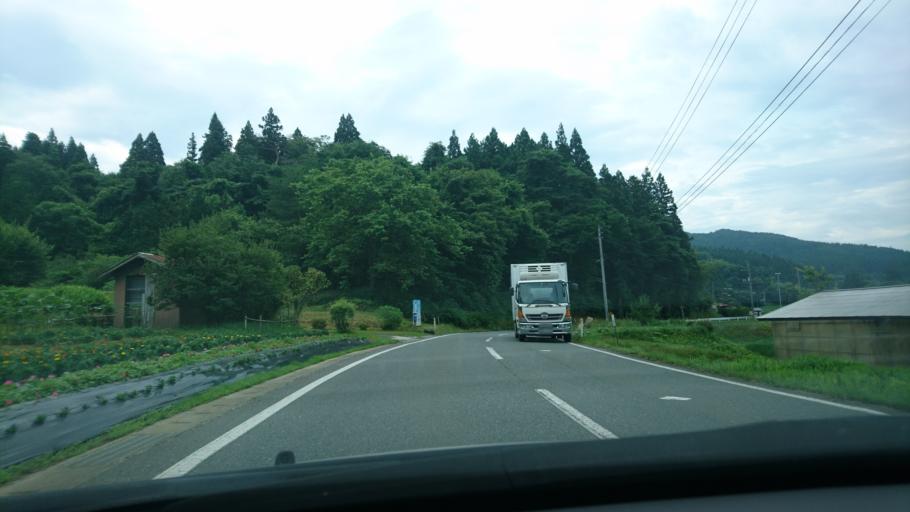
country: JP
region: Iwate
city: Ichinoseki
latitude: 38.8914
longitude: 141.4246
